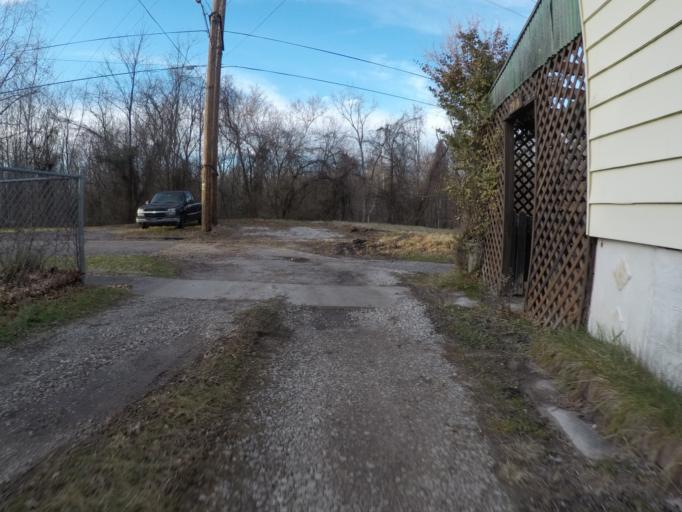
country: US
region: Ohio
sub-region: Lawrence County
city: Burlington
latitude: 38.4046
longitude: -82.4987
